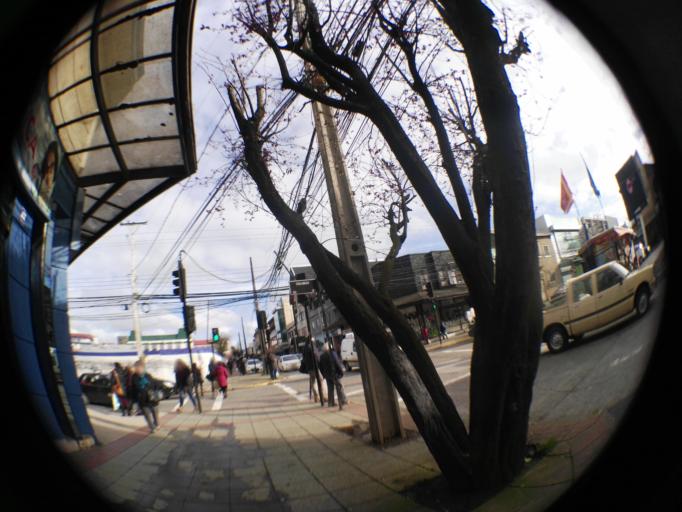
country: CL
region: Los Rios
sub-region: Provincia de Valdivia
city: Valdivia
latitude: -39.8132
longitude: -73.2437
